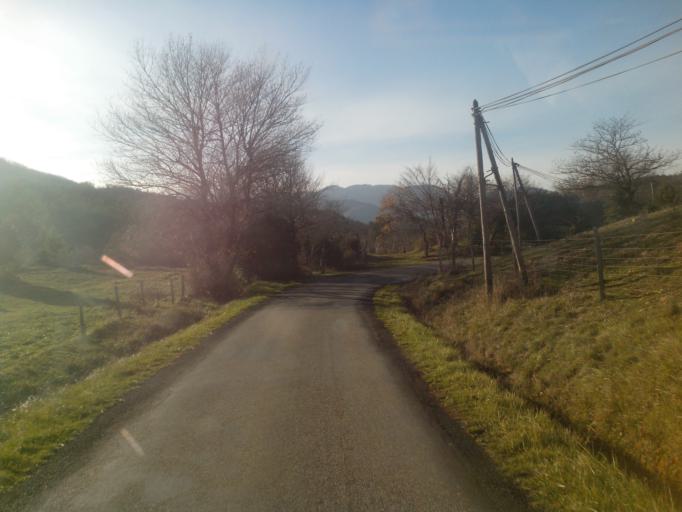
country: FR
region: Languedoc-Roussillon
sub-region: Departement des Pyrenees-Orientales
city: Saint-Paul-de-Fenouillet
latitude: 42.8788
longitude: 2.3816
